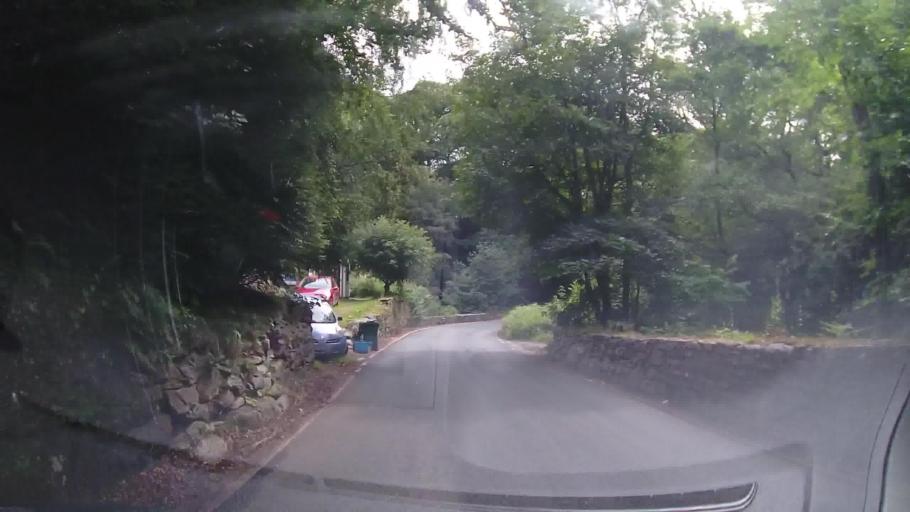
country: GB
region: Wales
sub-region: Gwynedd
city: Bala
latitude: 52.9068
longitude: -3.5216
